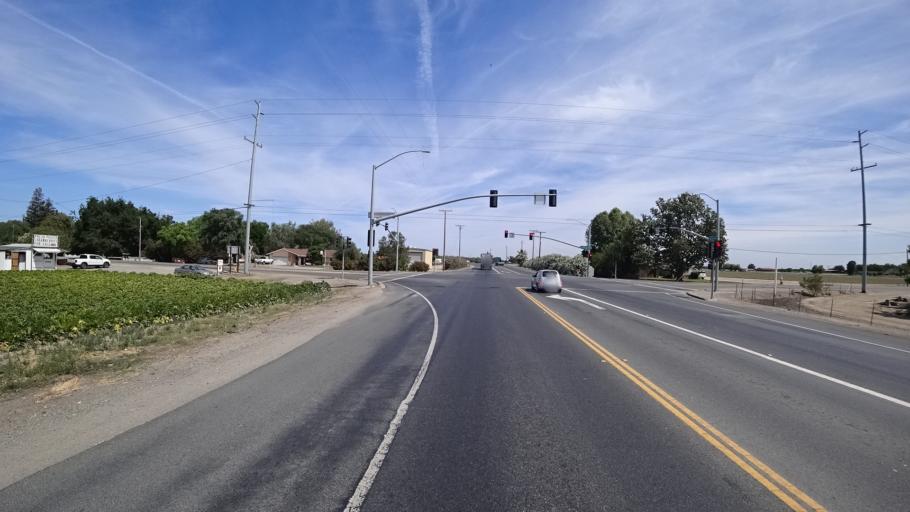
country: US
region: California
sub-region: Kings County
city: Hanford
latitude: 36.3421
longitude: -119.6010
